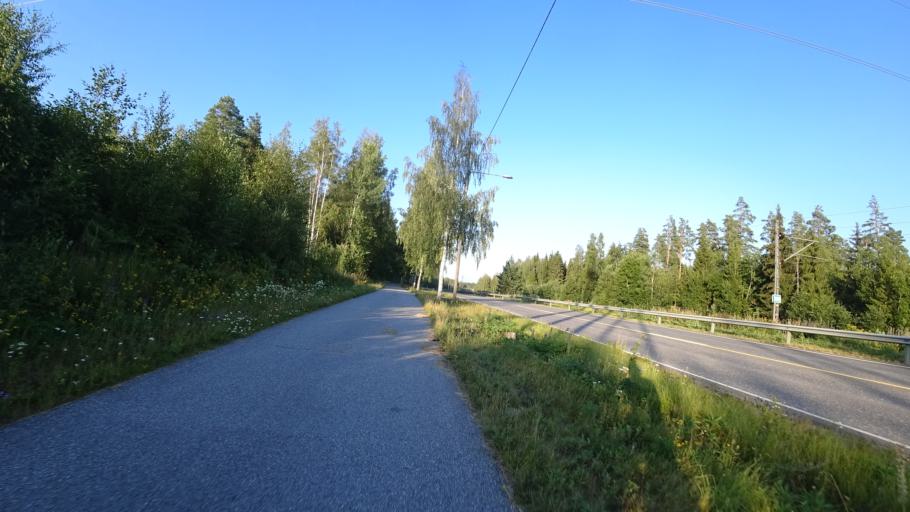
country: FI
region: Pirkanmaa
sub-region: Tampere
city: Nokia
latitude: 61.4665
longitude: 23.4340
